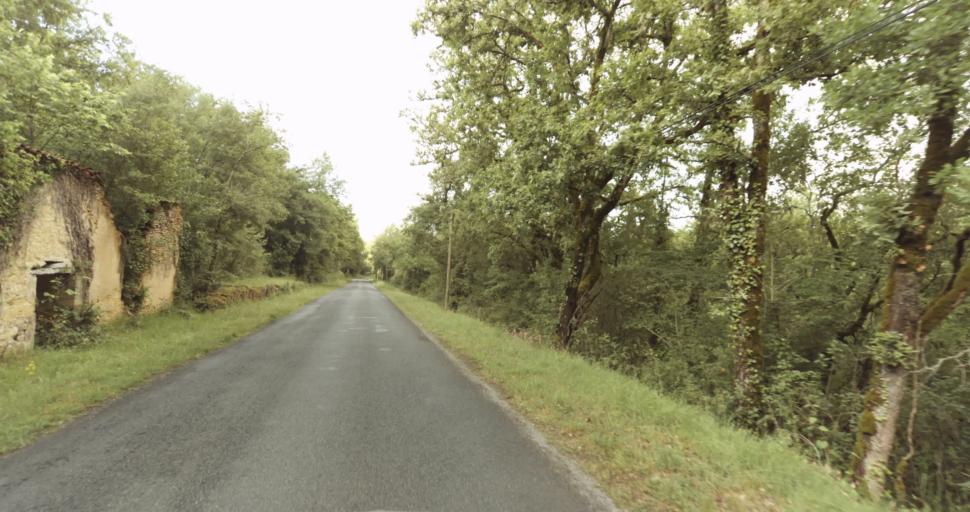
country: FR
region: Aquitaine
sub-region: Departement de la Dordogne
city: Lalinde
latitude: 44.9183
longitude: 0.8102
